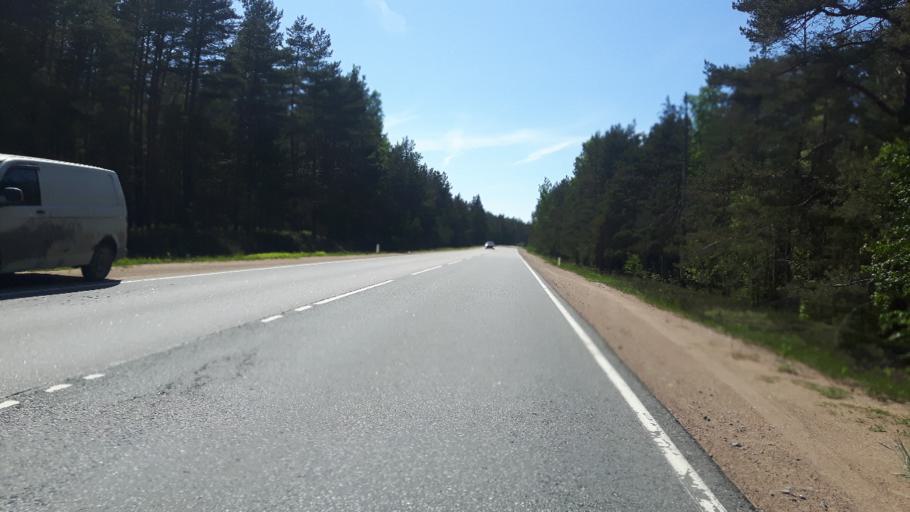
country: RU
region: Leningrad
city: Sista-Palkino
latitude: 59.7671
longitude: 28.7500
